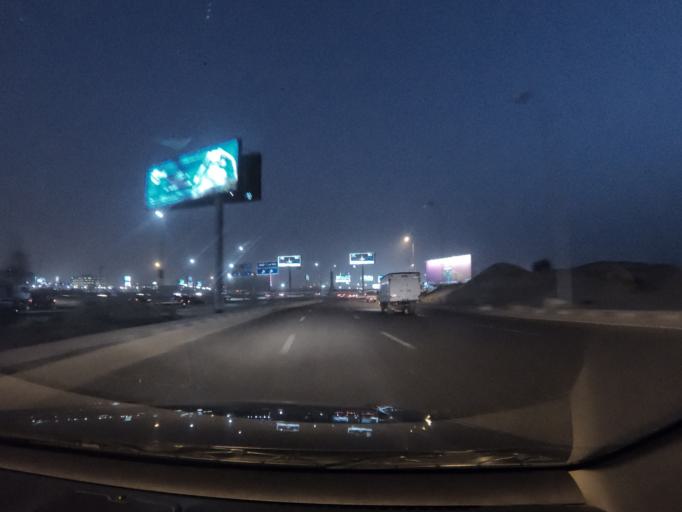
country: EG
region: Muhafazat al Qahirah
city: Cairo
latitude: 30.0212
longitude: 31.4010
